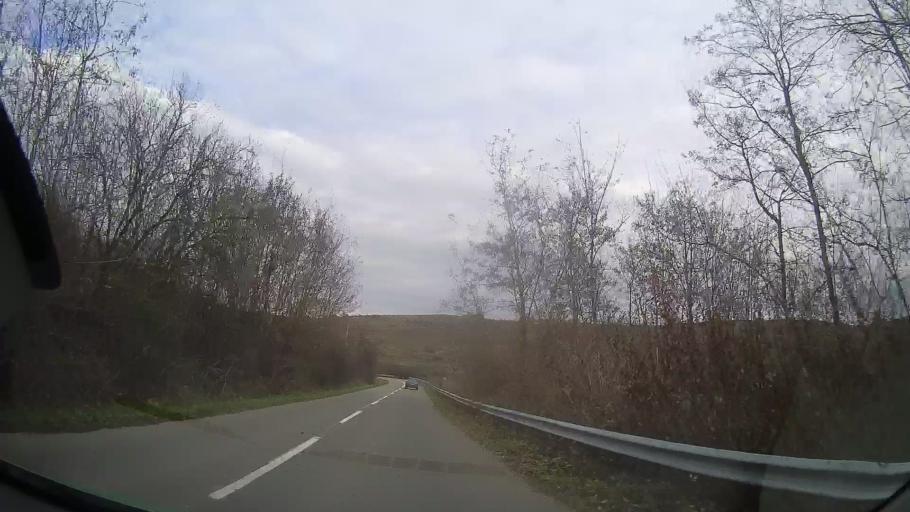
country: RO
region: Bistrita-Nasaud
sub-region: Comuna Milas
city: Milas
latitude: 46.8351
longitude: 24.4479
